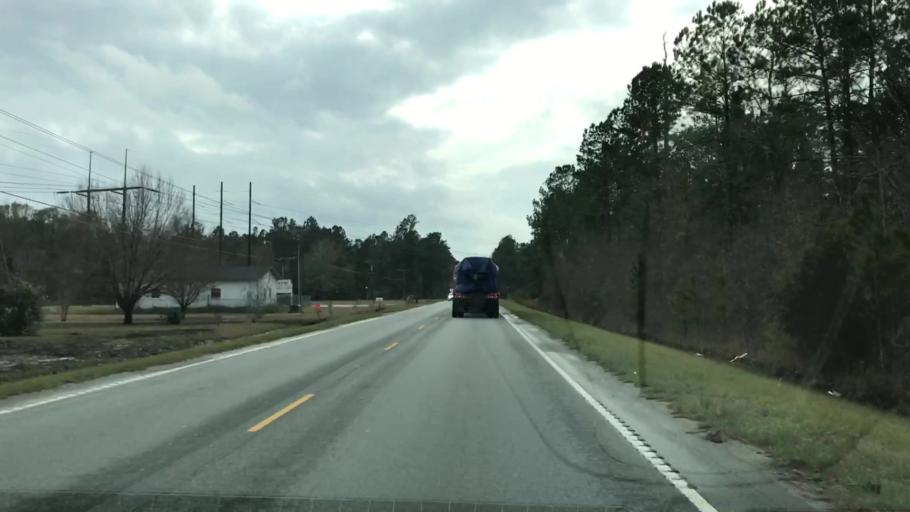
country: US
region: South Carolina
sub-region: Berkeley County
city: Bonneau Beach
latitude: 33.2613
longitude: -79.9274
